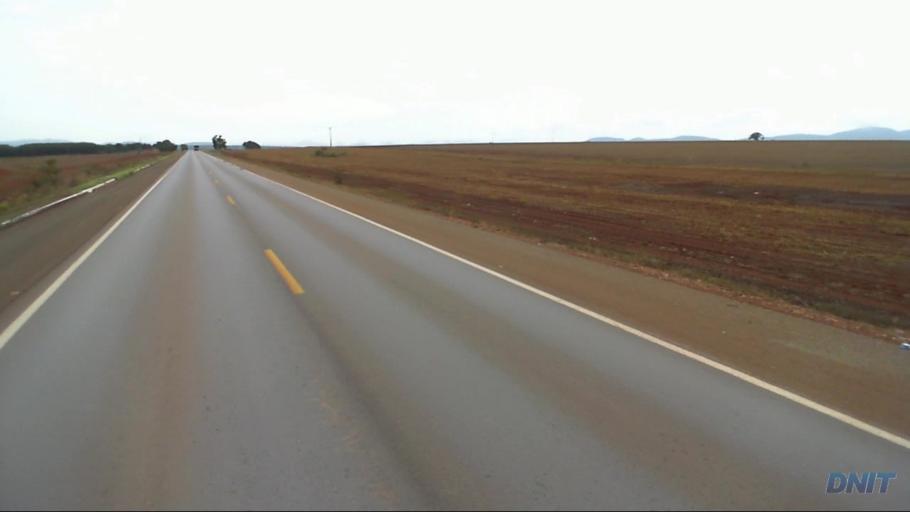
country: BR
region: Goias
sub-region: Uruacu
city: Uruacu
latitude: -14.6440
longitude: -49.1692
